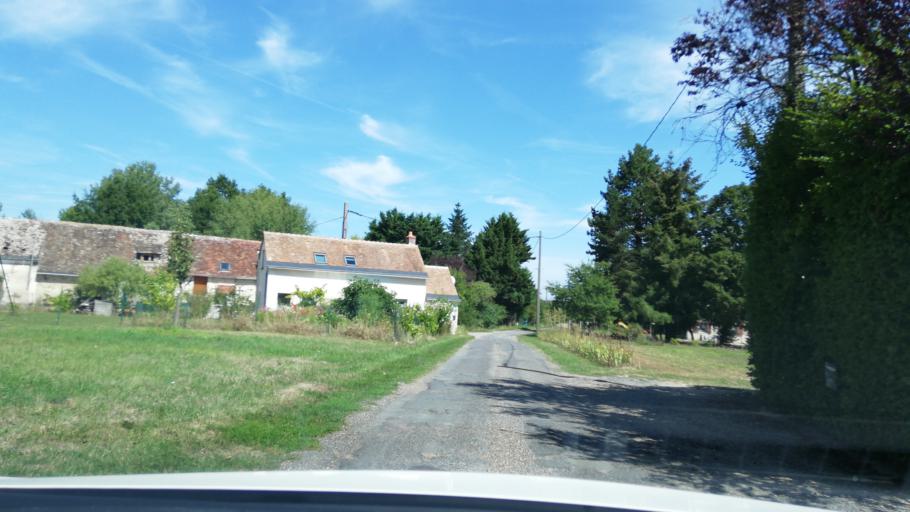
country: FR
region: Centre
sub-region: Departement d'Indre-et-Loire
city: Mazieres-de-Touraine
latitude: 47.3779
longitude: 0.4328
